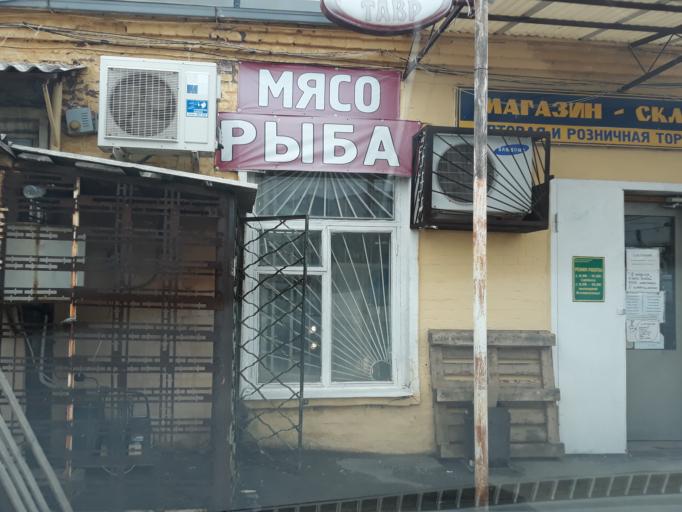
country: RU
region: Rostov
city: Taganrog
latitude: 47.2170
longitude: 38.8759
